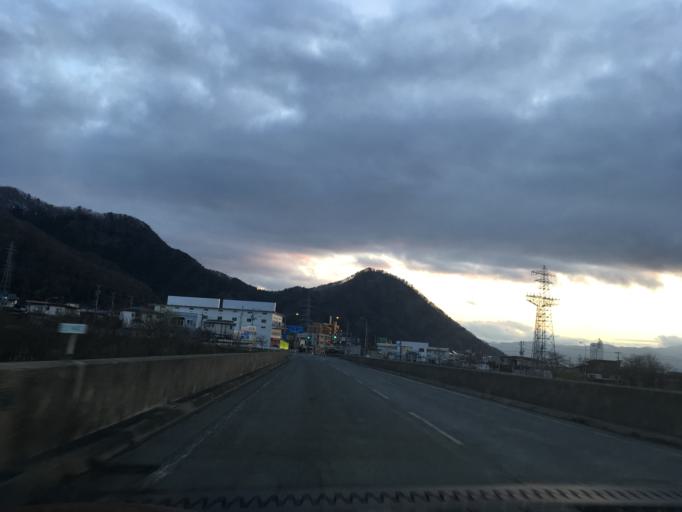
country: JP
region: Yamagata
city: Yamagata-shi
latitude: 38.2435
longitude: 140.3776
